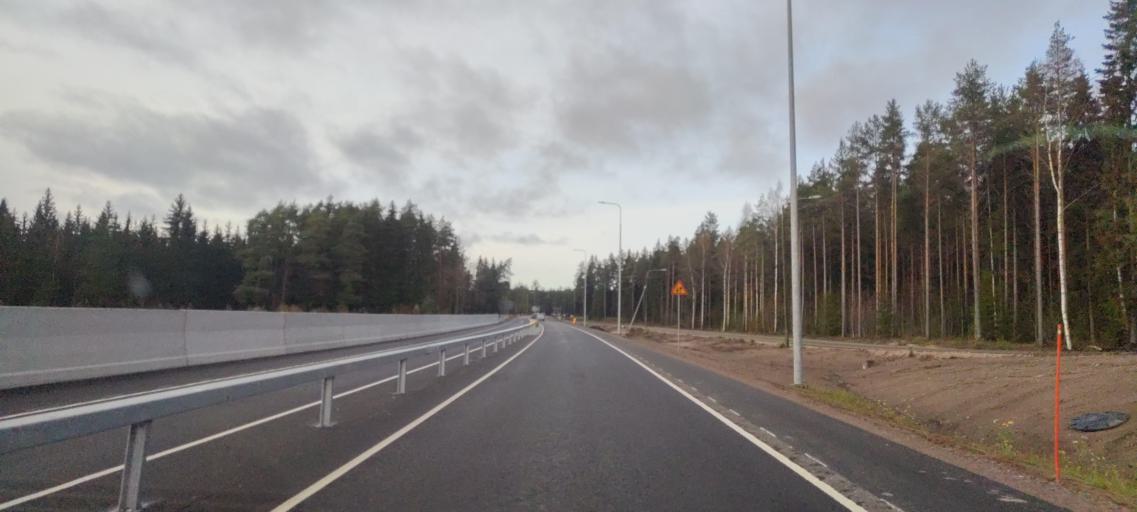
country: FI
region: Satakunta
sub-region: Rauma
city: Eurajoki
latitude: 61.2171
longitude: 21.7221
